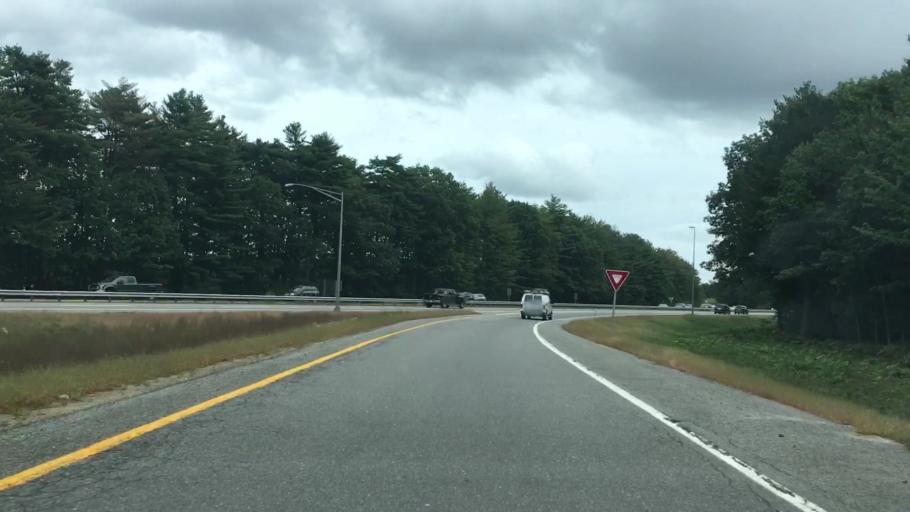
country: US
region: Maine
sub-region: Cumberland County
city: South Portland Gardens
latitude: 43.6284
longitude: -70.3346
